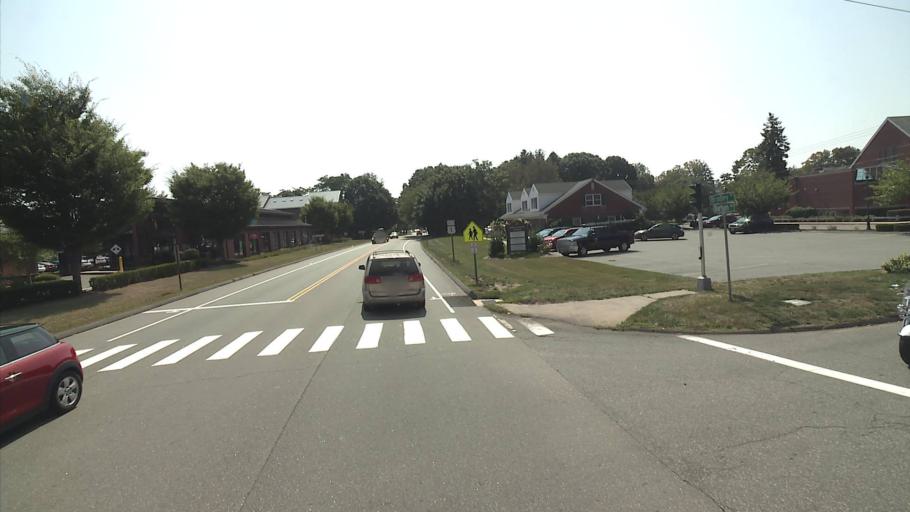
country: US
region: Connecticut
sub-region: New Haven County
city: Madison
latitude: 41.2817
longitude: -72.5995
